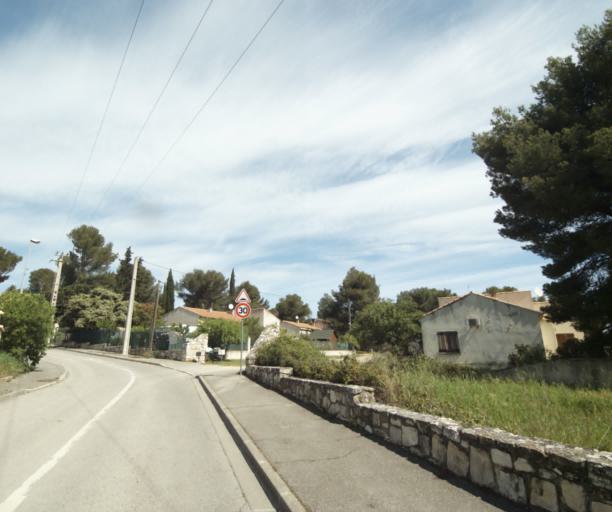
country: FR
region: Provence-Alpes-Cote d'Azur
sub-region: Departement des Bouches-du-Rhone
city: Rognac
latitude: 43.5153
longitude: 5.2195
